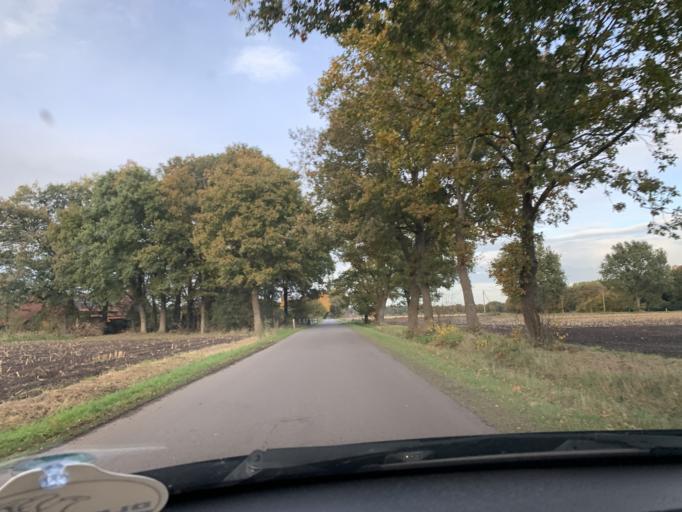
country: DE
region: Lower Saxony
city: Wiefelstede
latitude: 53.2375
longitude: 8.0536
